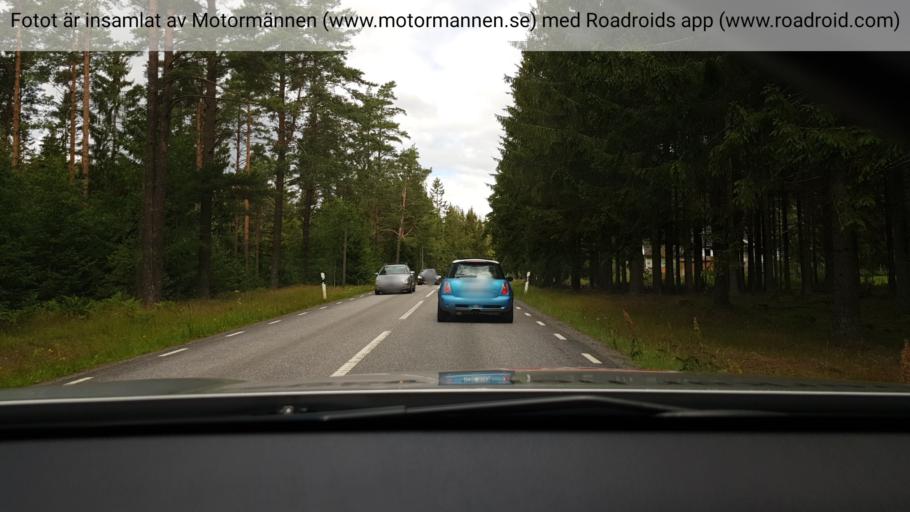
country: SE
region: Stockholm
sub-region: Haninge Kommun
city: Haninge
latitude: 59.1459
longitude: 18.1817
